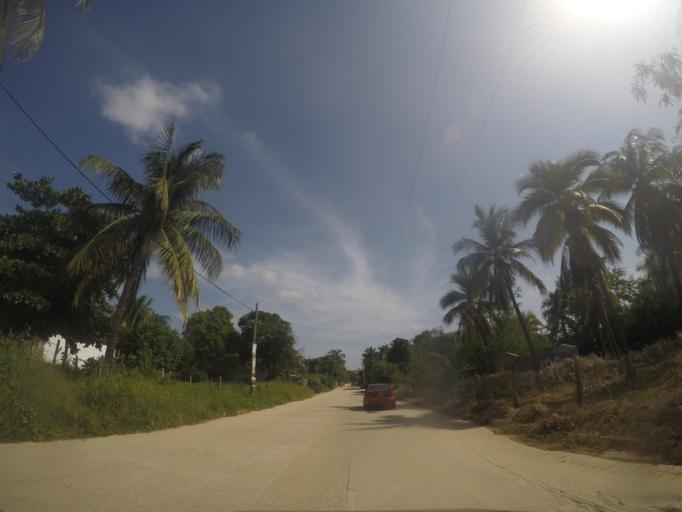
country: MX
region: Oaxaca
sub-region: Santa Maria Colotepec
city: Brisas de Zicatela
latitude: 15.8370
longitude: -97.0444
